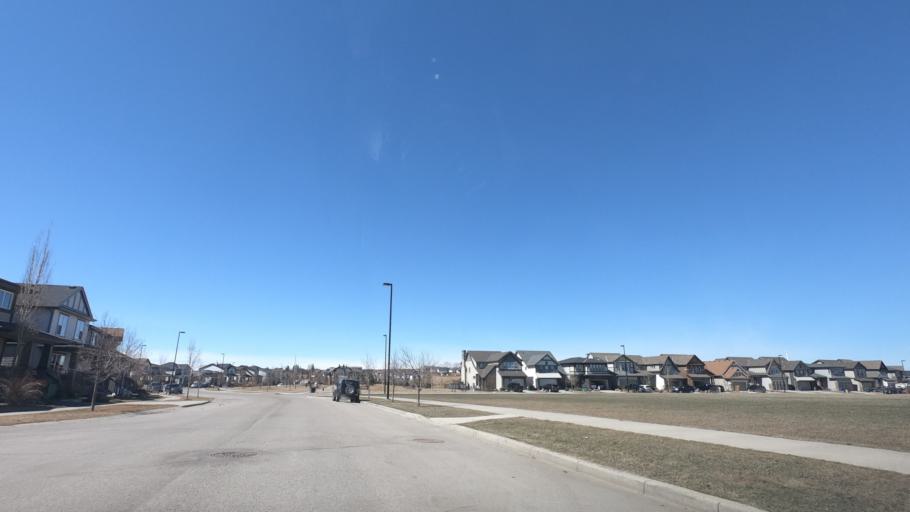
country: CA
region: Alberta
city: Airdrie
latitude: 51.3031
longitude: -114.0388
